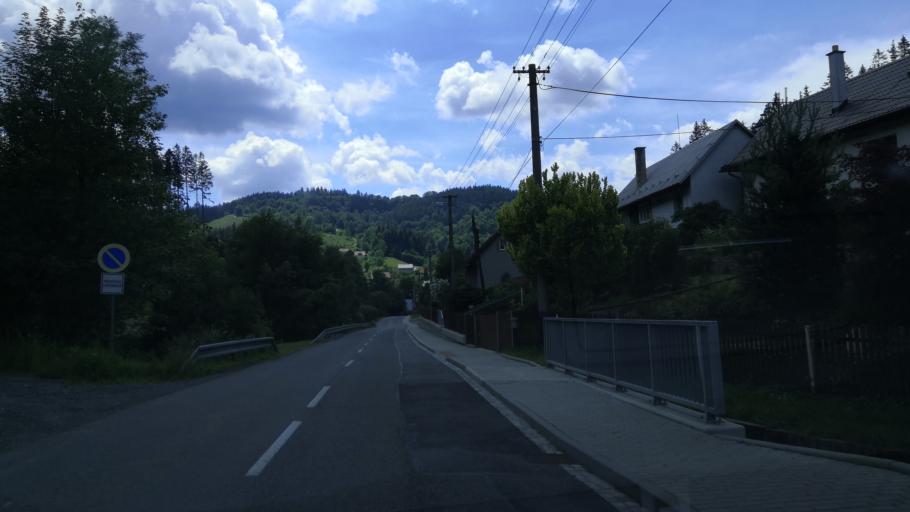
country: CZ
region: Zlin
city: Valasska Bystrice
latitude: 49.4171
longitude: 18.1137
